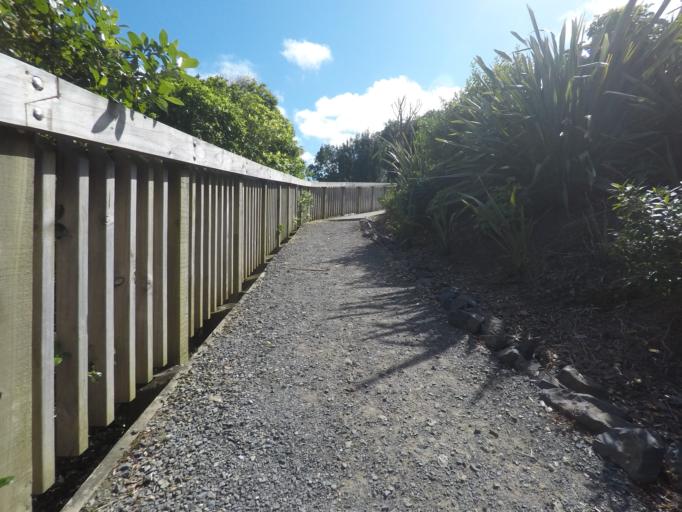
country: NZ
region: Auckland
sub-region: Auckland
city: Rosebank
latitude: -36.8559
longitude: 174.7123
